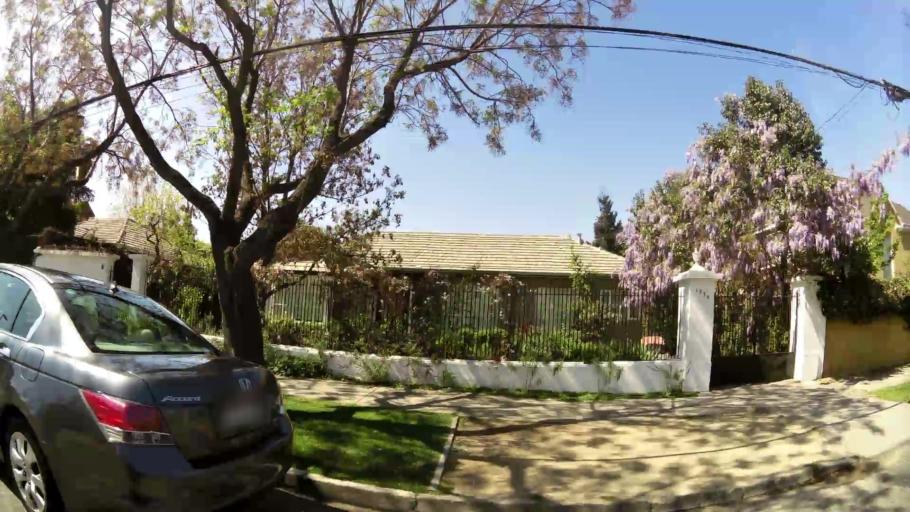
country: CL
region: Santiago Metropolitan
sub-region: Provincia de Santiago
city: Villa Presidente Frei, Nunoa, Santiago, Chile
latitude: -33.4239
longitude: -70.5605
